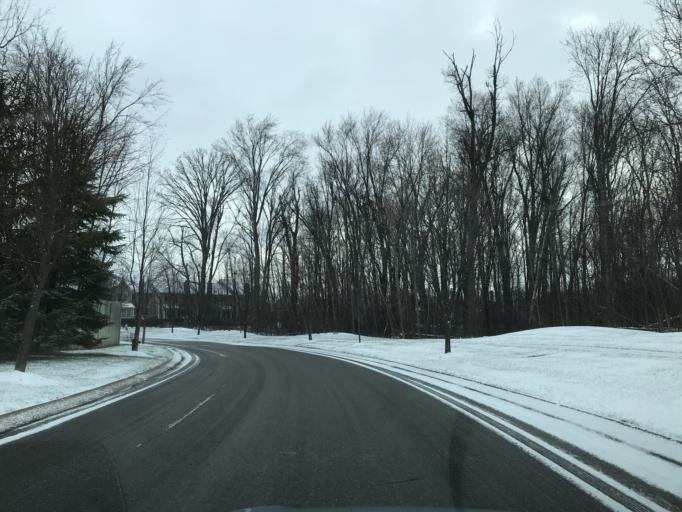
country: US
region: Michigan
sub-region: Oakland County
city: Wixom
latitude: 42.4805
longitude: -83.5447
